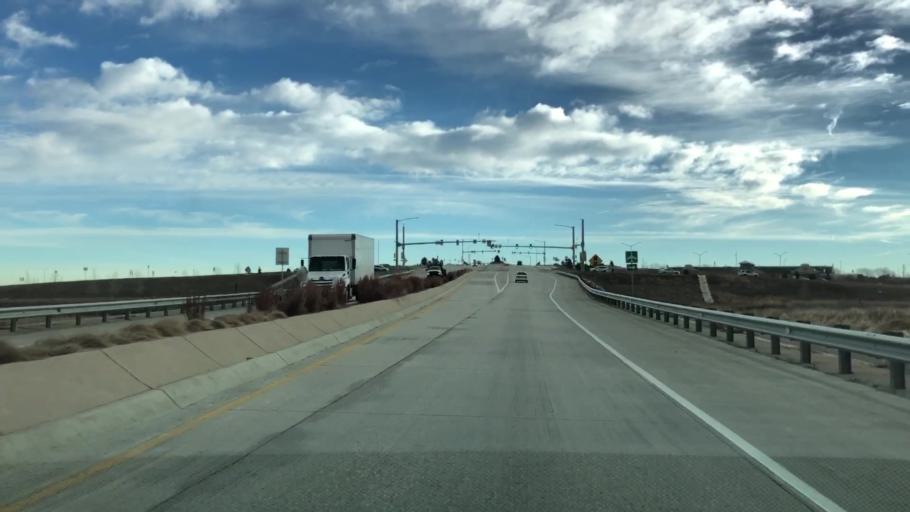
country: US
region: Colorado
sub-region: Weld County
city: Windsor
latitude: 40.4794
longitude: -104.9969
